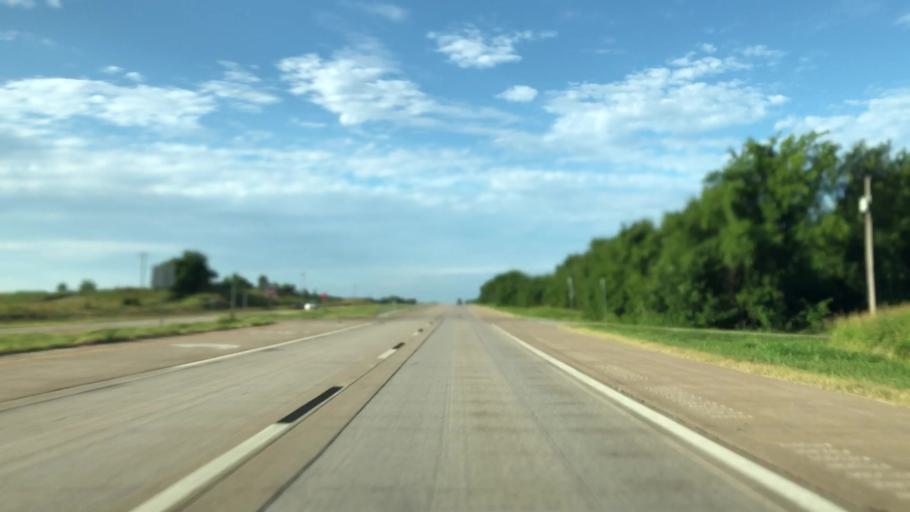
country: US
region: Oklahoma
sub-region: Osage County
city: Skiatook
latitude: 36.4387
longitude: -95.9207
